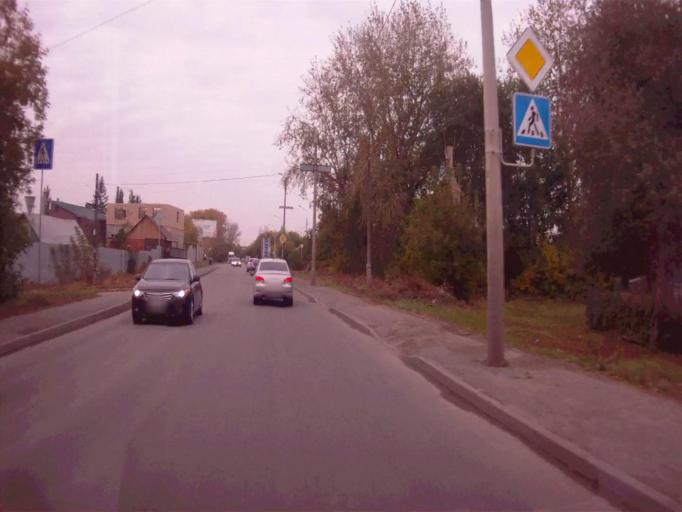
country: RU
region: Chelyabinsk
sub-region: Gorod Chelyabinsk
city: Chelyabinsk
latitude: 55.1354
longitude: 61.3916
